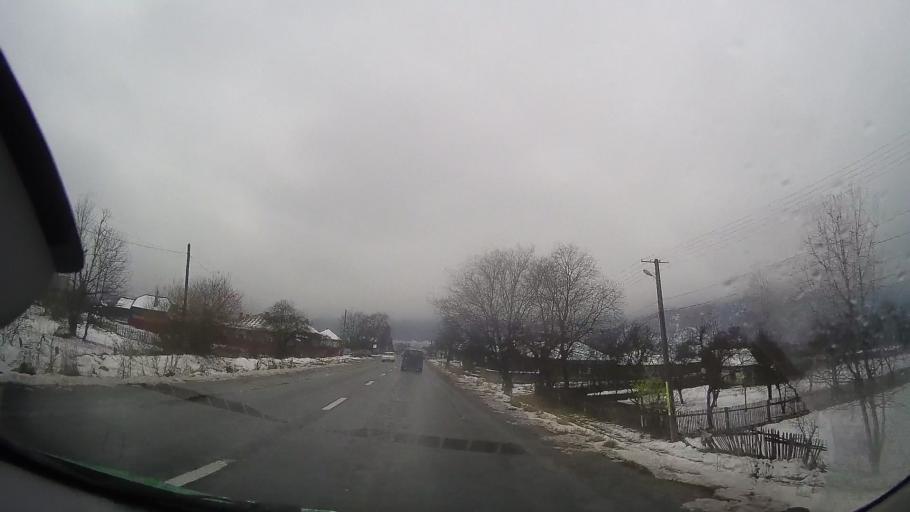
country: RO
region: Neamt
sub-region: Comuna Pangarati
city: Stejaru
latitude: 46.9144
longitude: 26.1848
